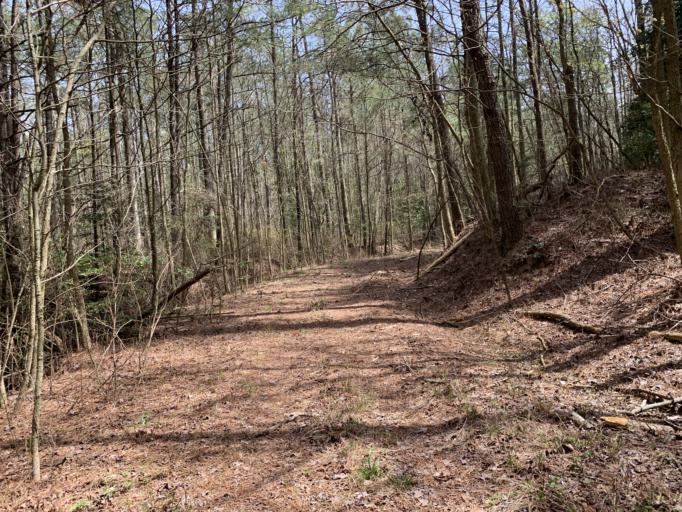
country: US
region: Delaware
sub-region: Sussex County
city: Millsboro
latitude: 38.5443
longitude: -75.3928
